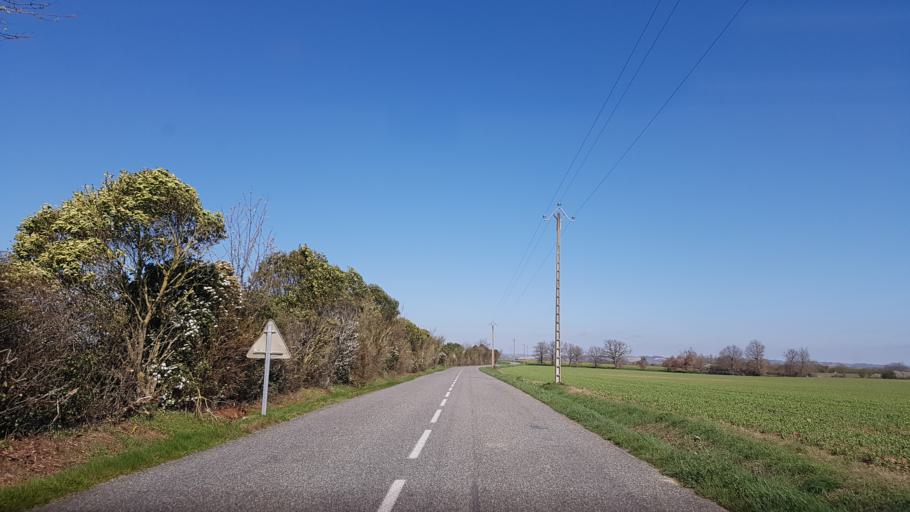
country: FR
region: Languedoc-Roussillon
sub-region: Departement de l'Aude
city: Belpech
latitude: 43.1608
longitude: 1.7092
